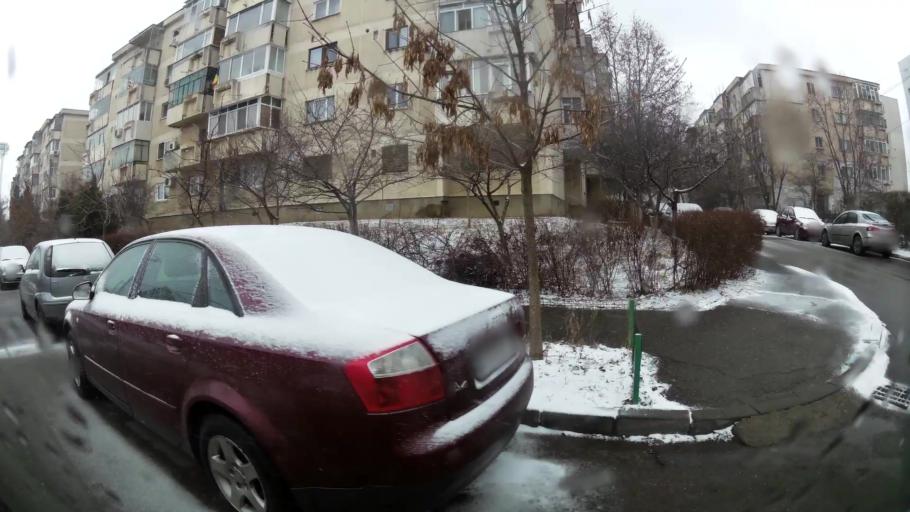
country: RO
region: Prahova
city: Ploiesti
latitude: 44.9300
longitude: 26.0075
